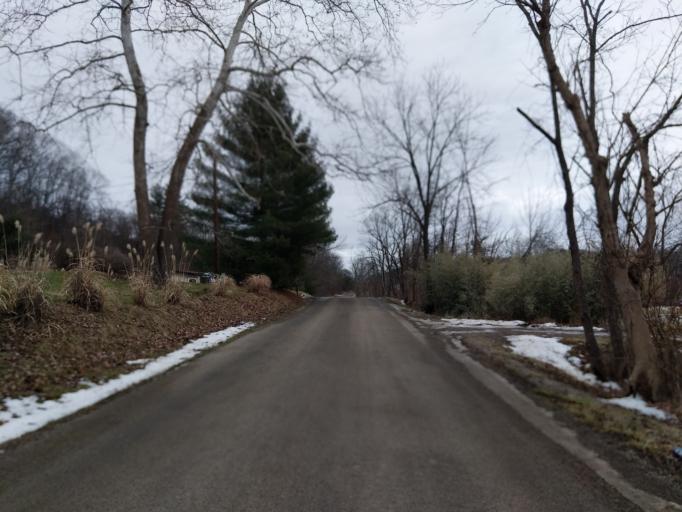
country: US
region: Ohio
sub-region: Athens County
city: The Plains
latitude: 39.3334
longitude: -82.1412
